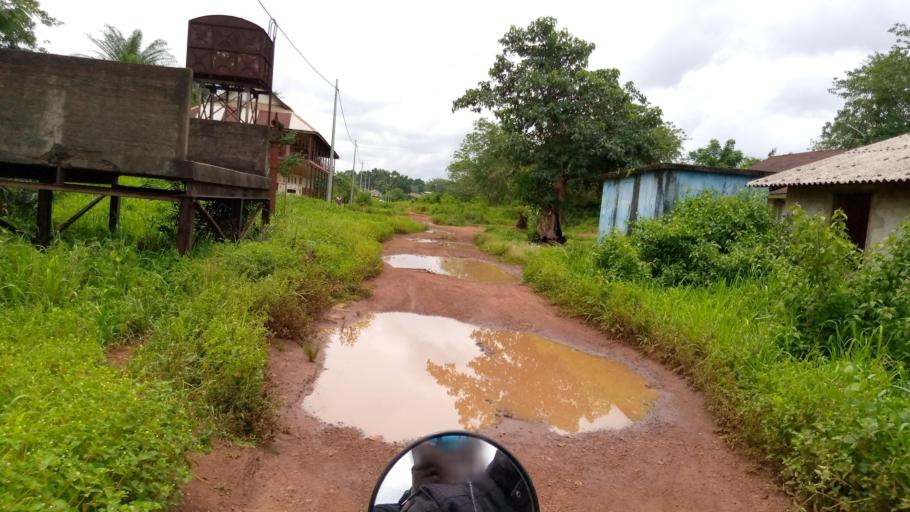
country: SL
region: Southern Province
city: Rotifunk
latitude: 8.1900
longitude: -12.5726
